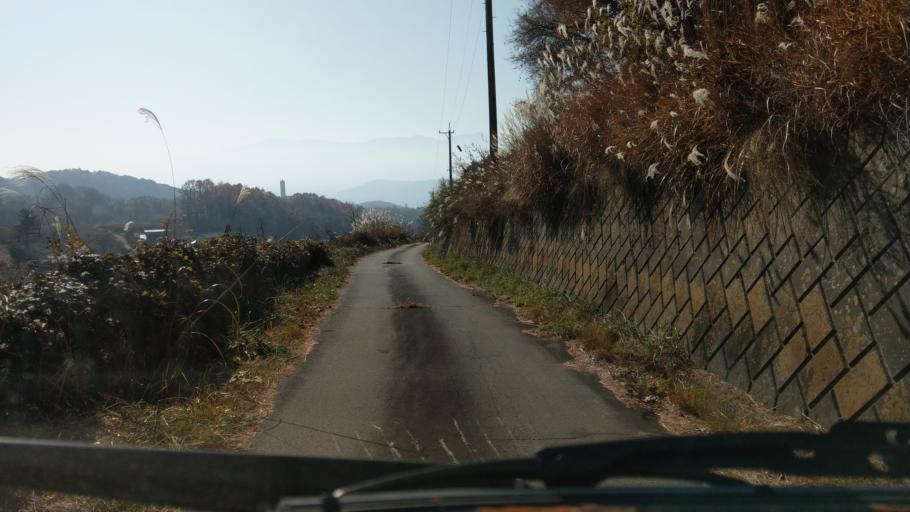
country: JP
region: Nagano
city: Komoro
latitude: 36.3591
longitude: 138.4381
